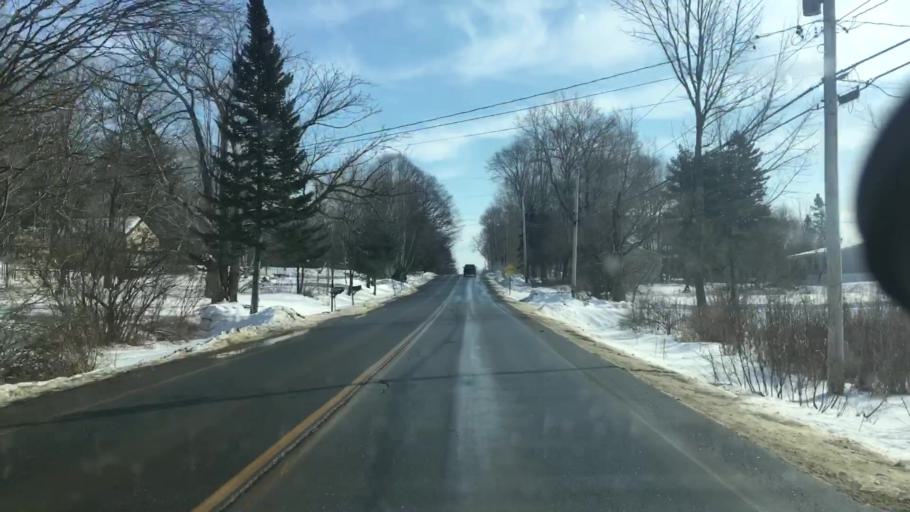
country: US
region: Maine
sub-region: Penobscot County
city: Bangor
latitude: 44.8498
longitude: -68.8414
